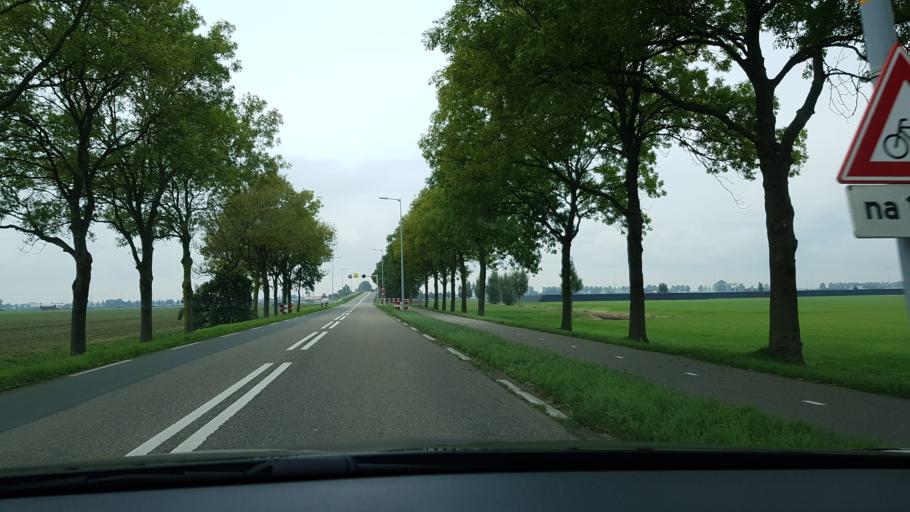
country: NL
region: South Holland
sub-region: Gemeente Kaag en Braassem
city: Leimuiden
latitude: 52.2438
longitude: 4.6731
